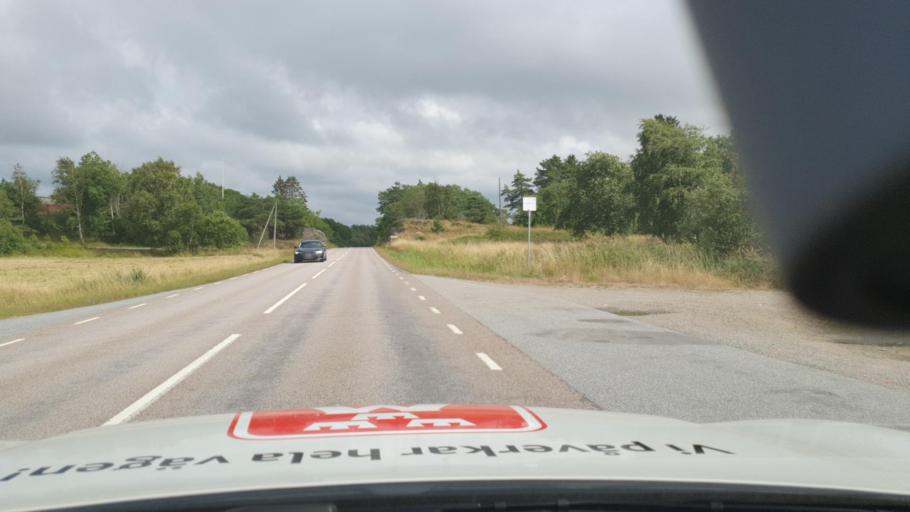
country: SE
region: Vaestra Goetaland
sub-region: Tanums Kommun
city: Grebbestad
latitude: 58.5956
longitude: 11.3072
